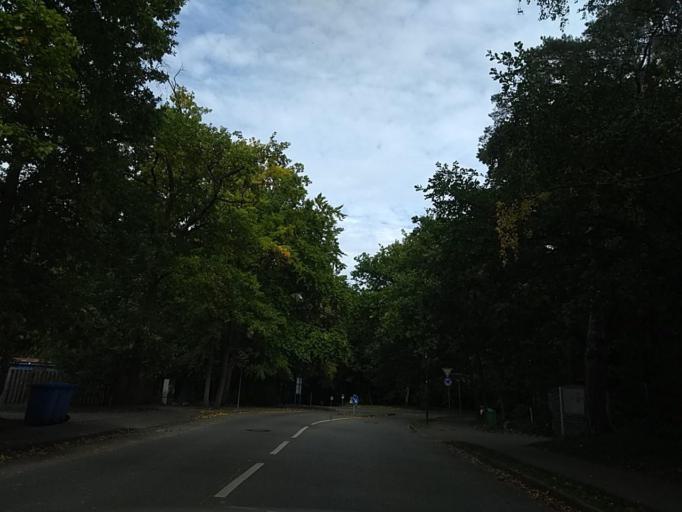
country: DE
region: Mecklenburg-Vorpommern
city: Seeheilbad Graal-Muritz
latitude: 54.2521
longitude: 12.2434
